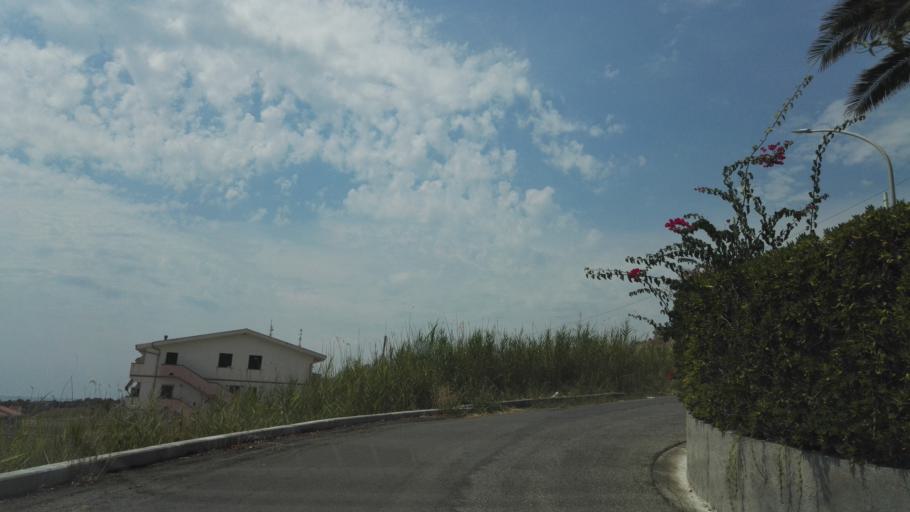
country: IT
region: Calabria
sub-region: Provincia di Reggio Calabria
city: Riace Marina
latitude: 38.3857
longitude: 16.5225
